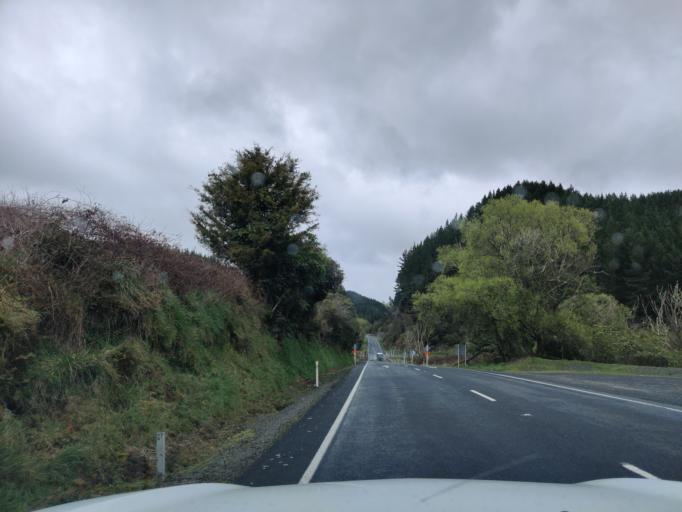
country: NZ
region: Waikato
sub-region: Otorohanga District
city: Otorohanga
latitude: -38.6519
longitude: 175.2078
